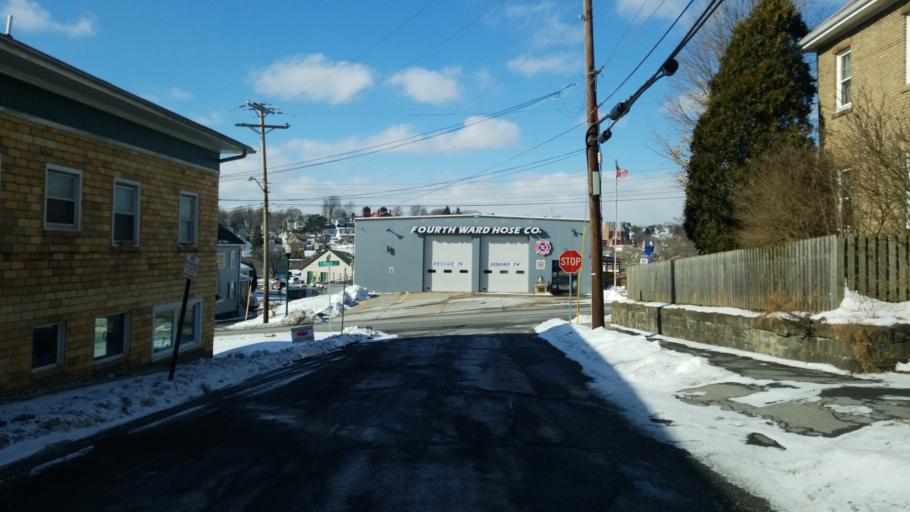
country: US
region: Pennsylvania
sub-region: Clearfield County
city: DuBois
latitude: 41.1158
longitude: -78.7659
